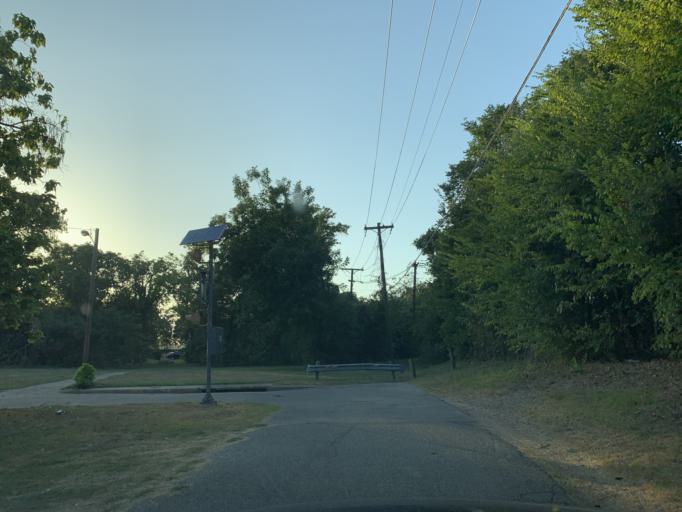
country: US
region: Texas
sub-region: Dallas County
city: Dallas
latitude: 32.7540
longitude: -96.7470
